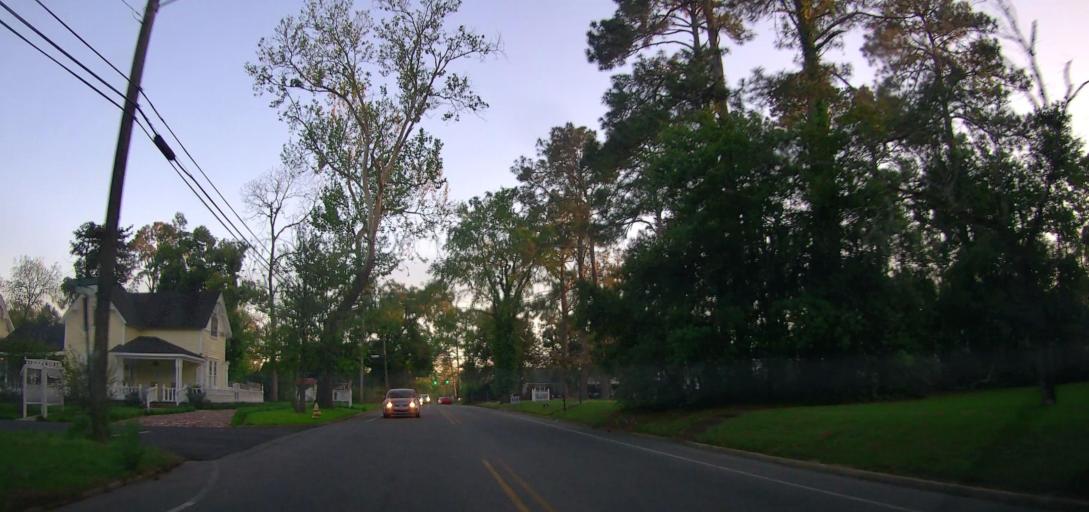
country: US
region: Georgia
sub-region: Ben Hill County
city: Fitzgerald
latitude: 31.7158
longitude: -83.2654
